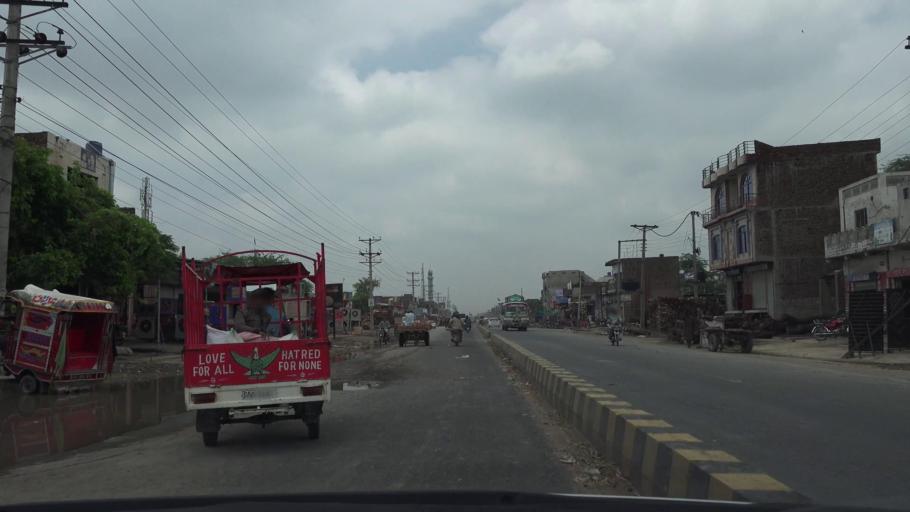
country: PK
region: Punjab
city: Faisalabad
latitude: 31.3901
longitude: 73.1916
